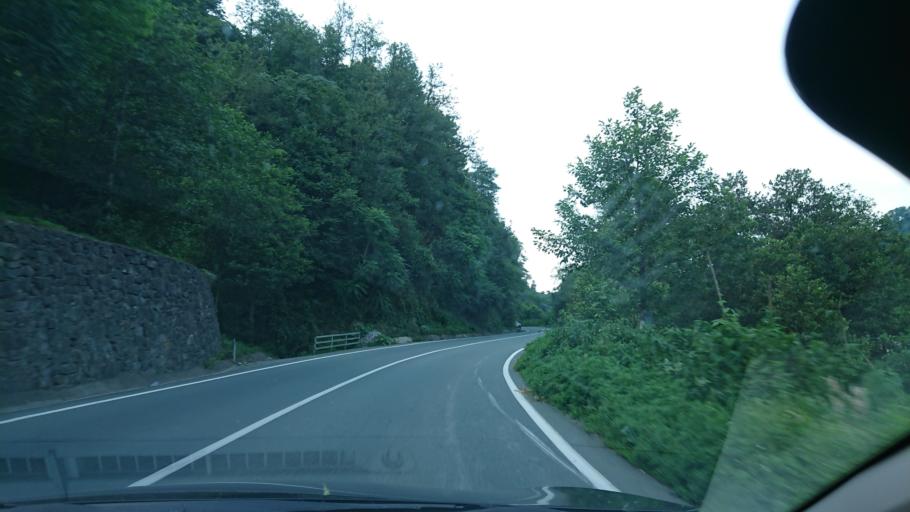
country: TR
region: Rize
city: Cayeli
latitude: 41.0731
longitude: 40.7111
